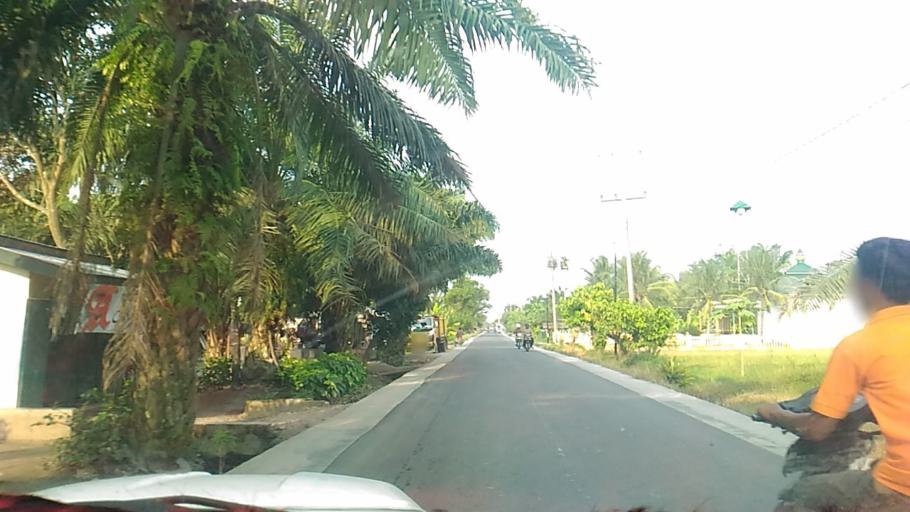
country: ID
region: North Sumatra
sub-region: Kabupaten Langkat
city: Stabat
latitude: 3.7031
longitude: 98.5186
